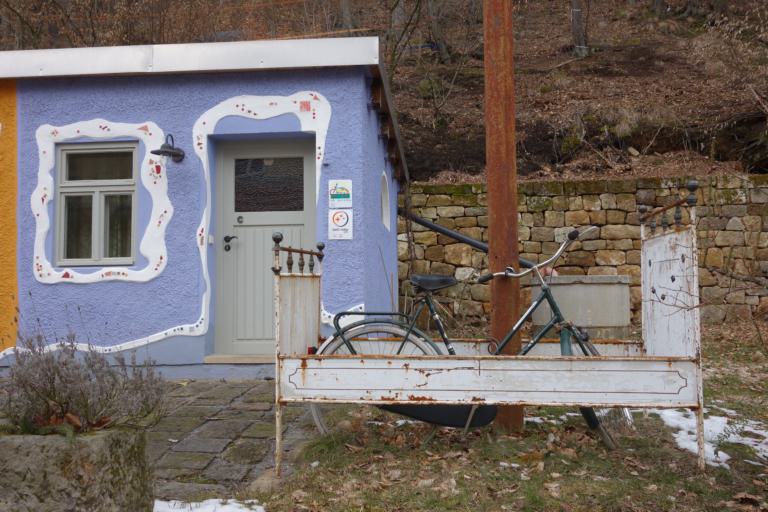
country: DE
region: Saxony
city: Stadt Wehlen
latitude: 50.9527
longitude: 14.0190
